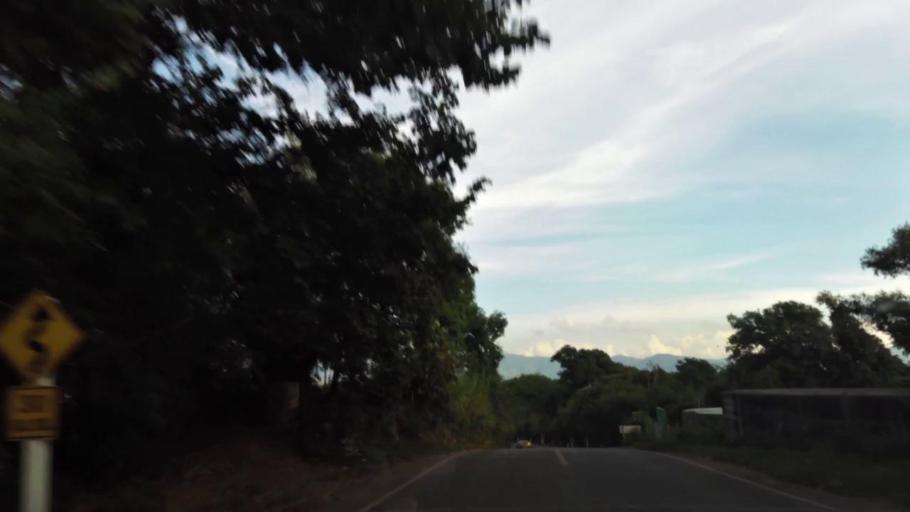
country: TH
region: Chiang Rai
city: Khun Tan
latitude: 19.8728
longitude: 100.3465
